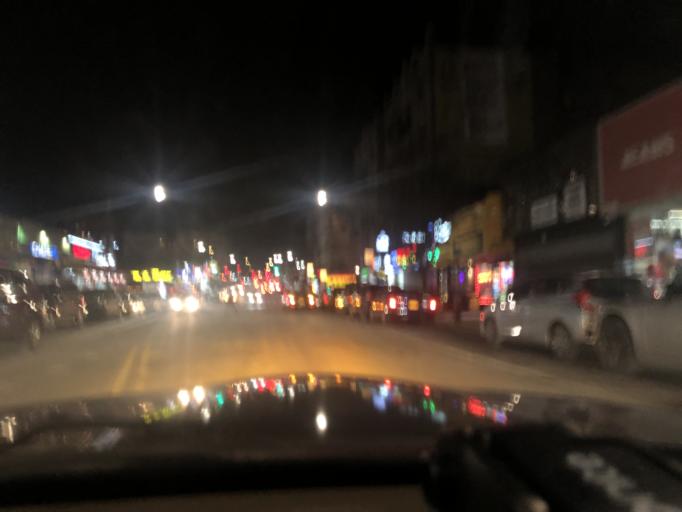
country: US
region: New York
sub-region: New York County
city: Inwood
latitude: 40.8662
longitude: -73.9202
